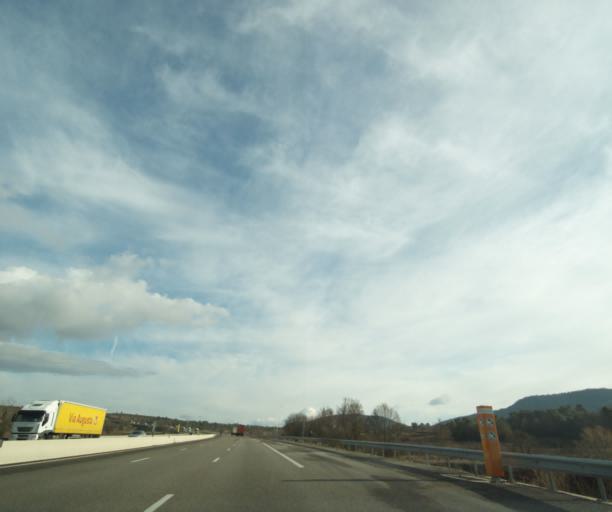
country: FR
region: Provence-Alpes-Cote d'Azur
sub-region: Departement du Var
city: Pourrieres
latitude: 43.4735
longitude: 5.7885
